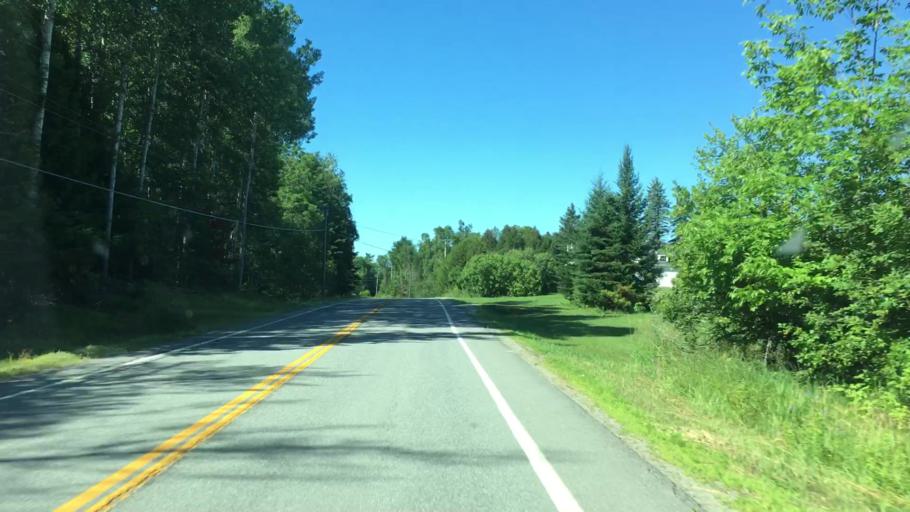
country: US
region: Maine
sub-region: Hancock County
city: Dedham
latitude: 44.6871
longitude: -68.6627
